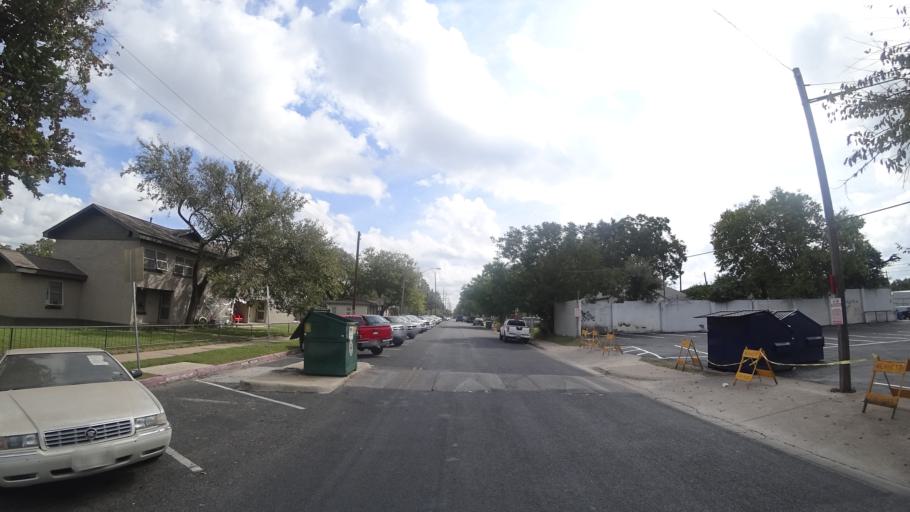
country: US
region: Texas
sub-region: Travis County
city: Austin
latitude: 30.2558
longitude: -97.7178
